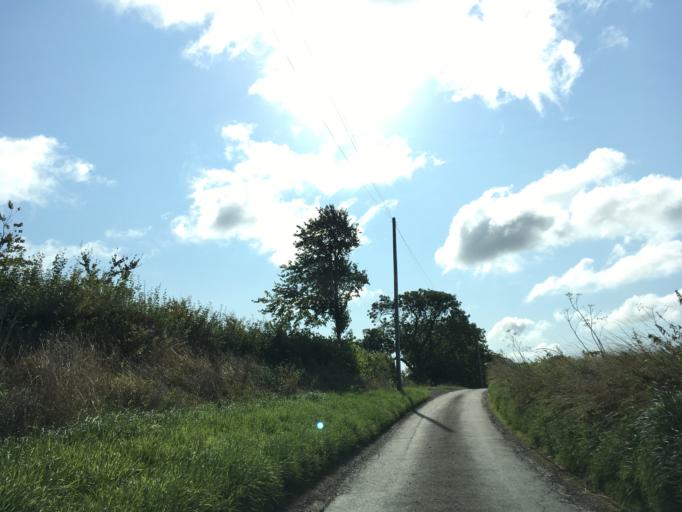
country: GB
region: England
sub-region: South Gloucestershire
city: Hinton
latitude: 51.5099
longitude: -2.3611
